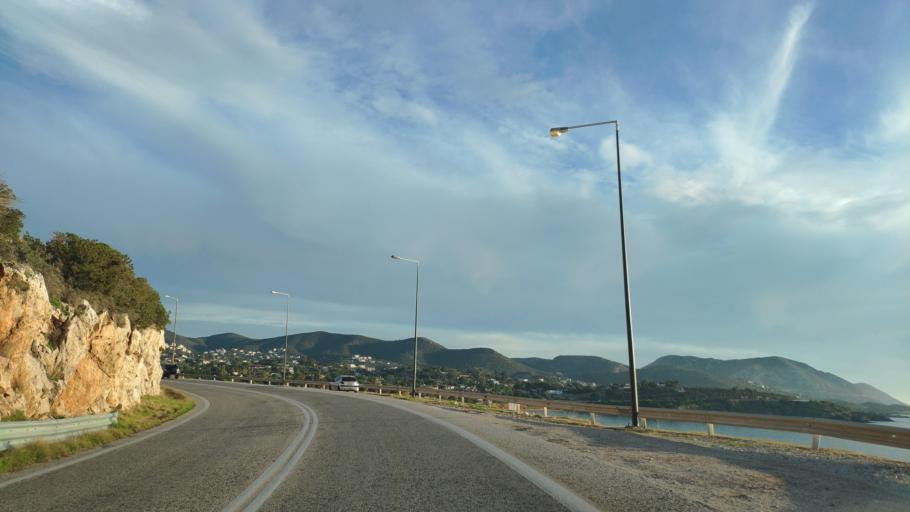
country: GR
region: Attica
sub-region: Nomarchia Anatolikis Attikis
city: Palaia Fokaia
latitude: 37.7062
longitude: 23.9365
